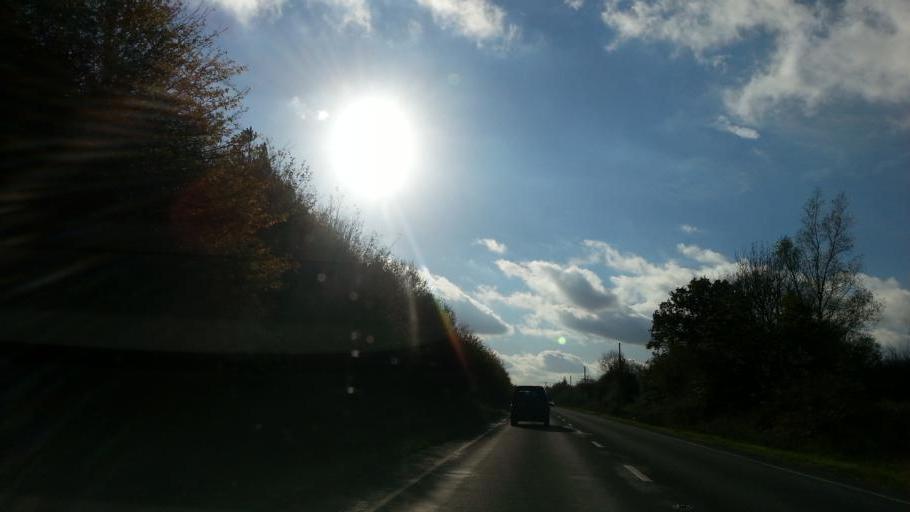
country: GB
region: England
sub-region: Norfolk
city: Harleston
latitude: 52.3809
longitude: 1.2575
